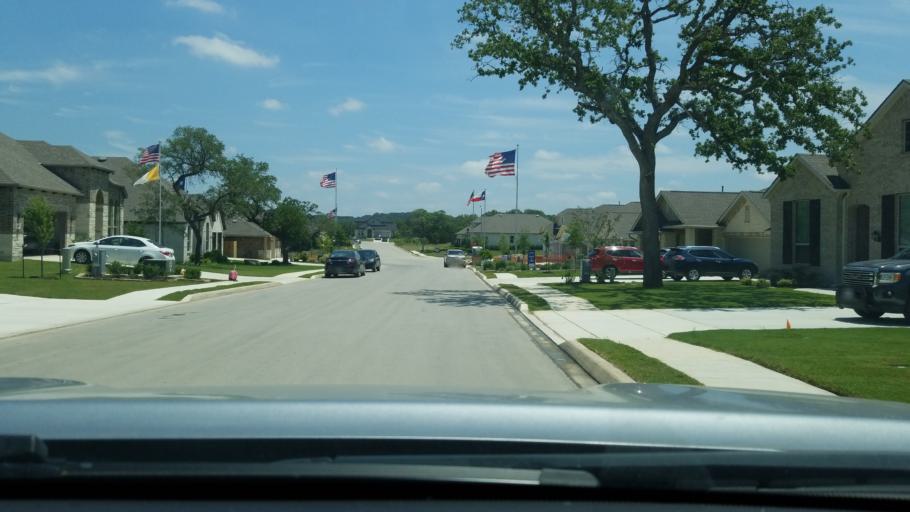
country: US
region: Texas
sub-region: Comal County
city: Bulverde
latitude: 29.8055
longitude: -98.5162
